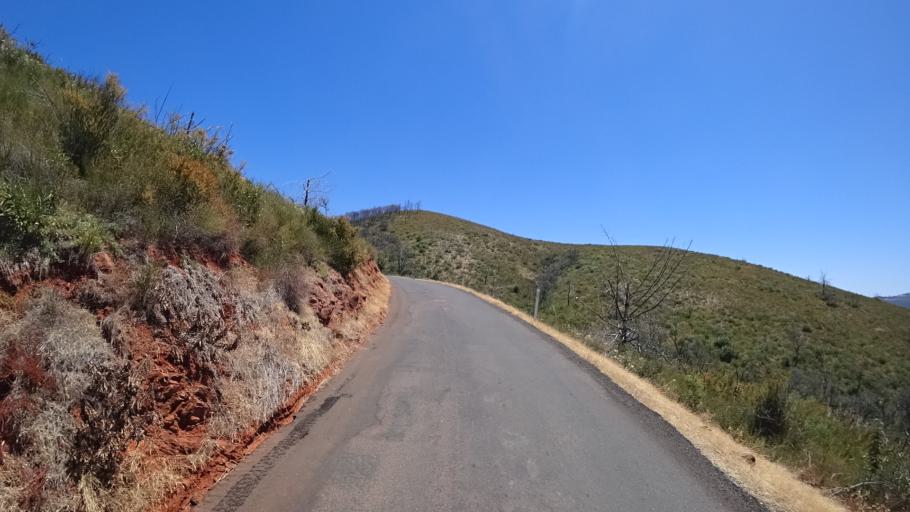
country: US
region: California
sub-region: Calaveras County
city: Mountain Ranch
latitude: 38.2894
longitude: -120.6102
